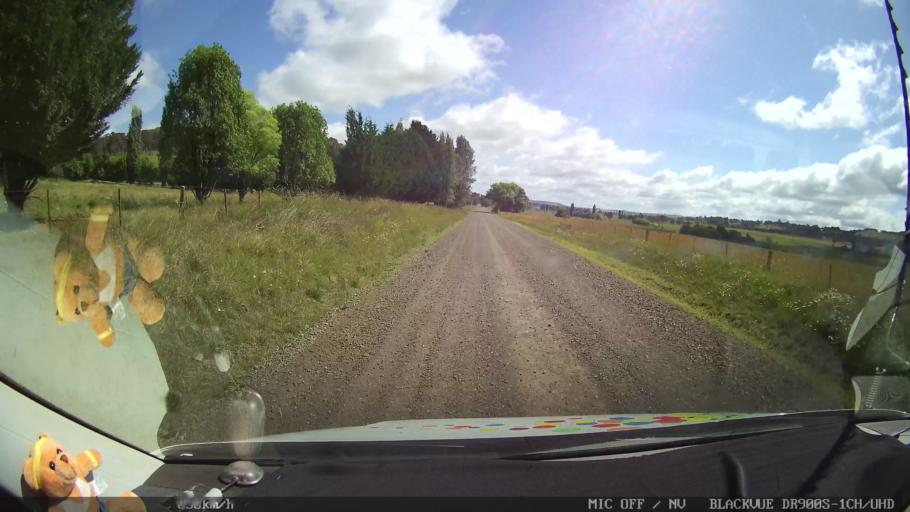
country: AU
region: New South Wales
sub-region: Glen Innes Severn
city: Glen Innes
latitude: -29.9605
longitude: 151.7009
